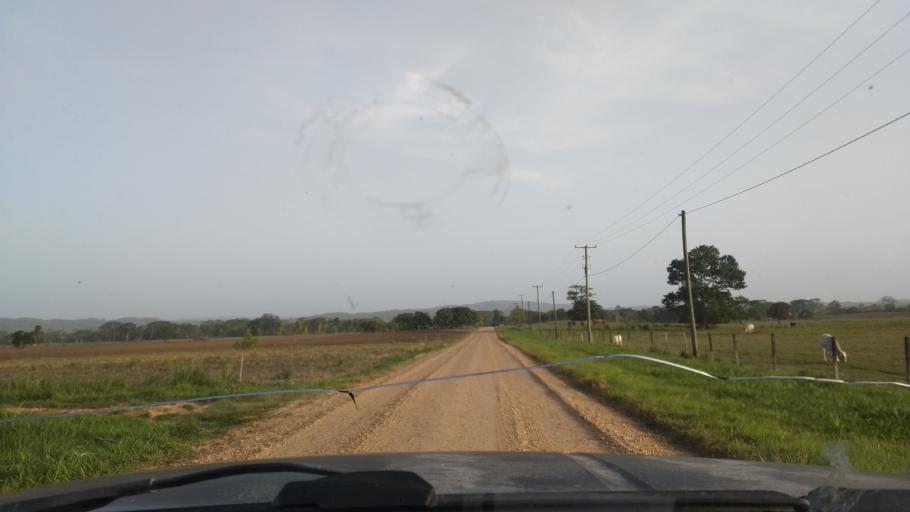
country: BZ
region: Cayo
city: San Ignacio
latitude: 17.2147
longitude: -89.0137
